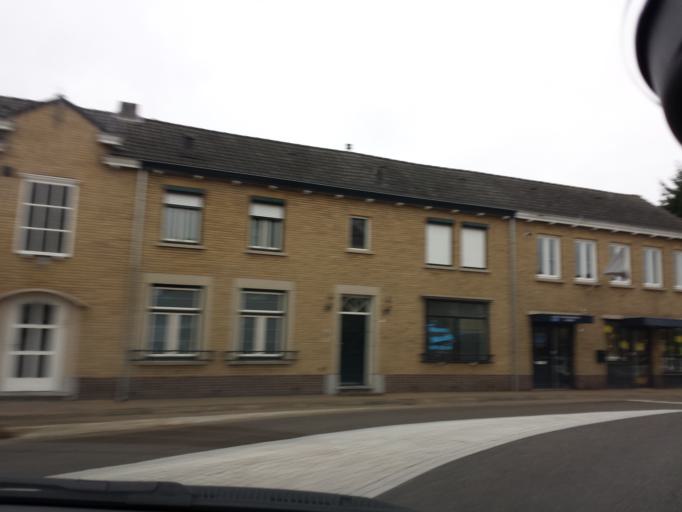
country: NL
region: Limburg
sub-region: Gemeente Sittard-Geleen
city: Born
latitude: 51.0643
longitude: 5.8527
